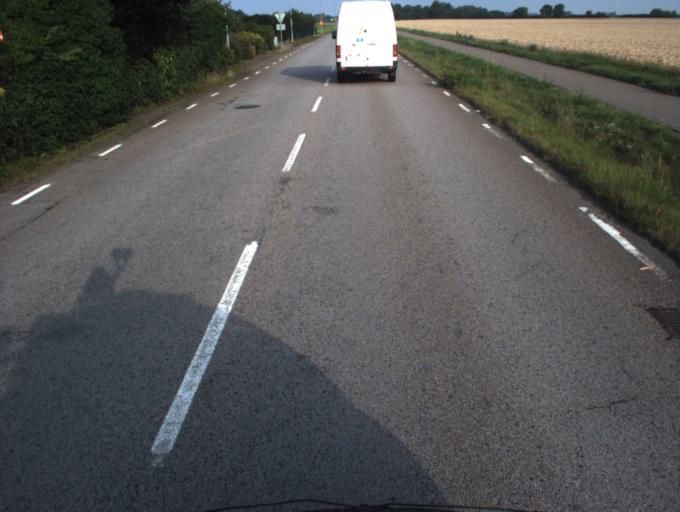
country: SE
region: Skane
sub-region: Angelholms Kommun
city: Strovelstorp
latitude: 56.1378
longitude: 12.8105
